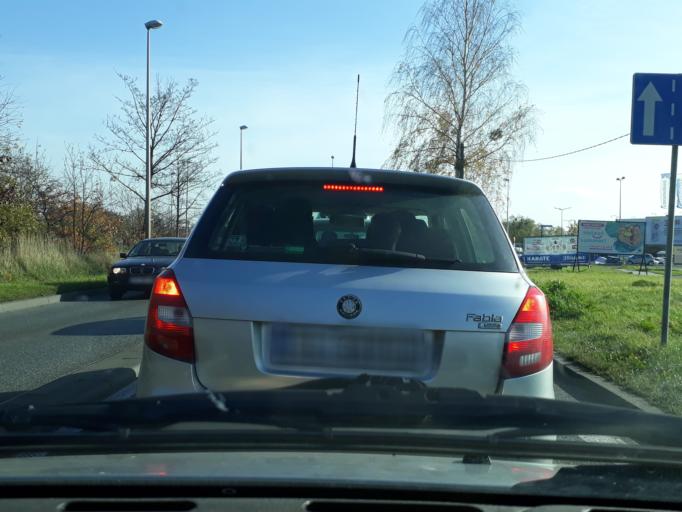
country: PL
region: Silesian Voivodeship
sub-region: Powiat tarnogorski
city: Tarnowskie Gory
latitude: 50.4382
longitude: 18.8411
